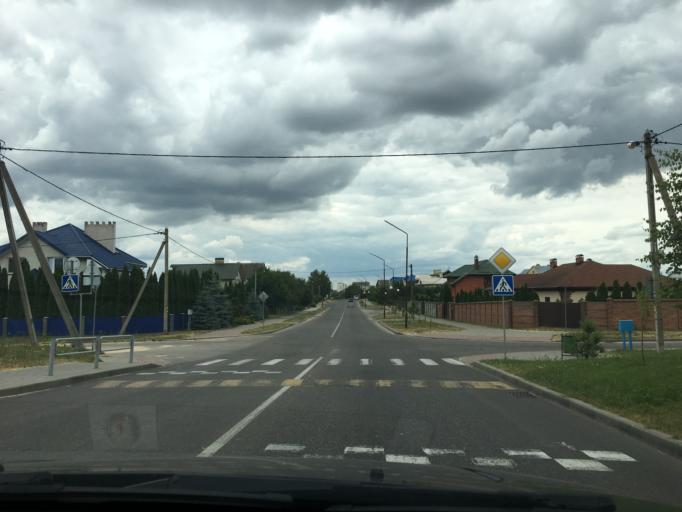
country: BY
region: Grodnenskaya
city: Hrodna
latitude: 53.6216
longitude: 23.8390
